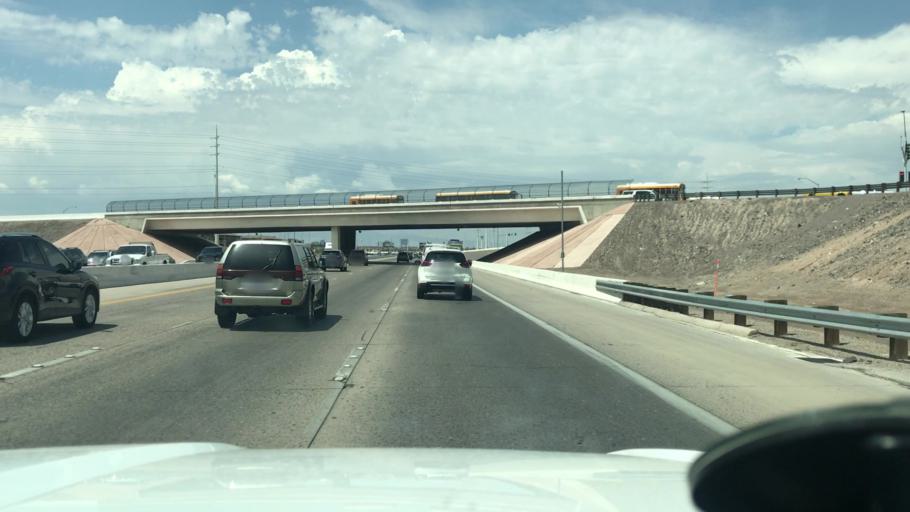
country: US
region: Nevada
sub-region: Clark County
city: Whitney
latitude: 36.0828
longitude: -115.0484
